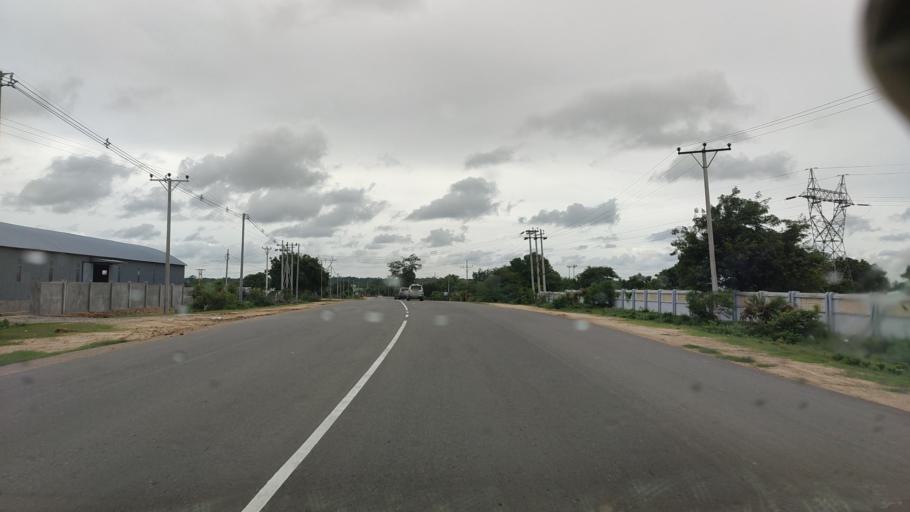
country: MM
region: Mandalay
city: Meiktila
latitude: 20.8332
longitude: 95.8990
